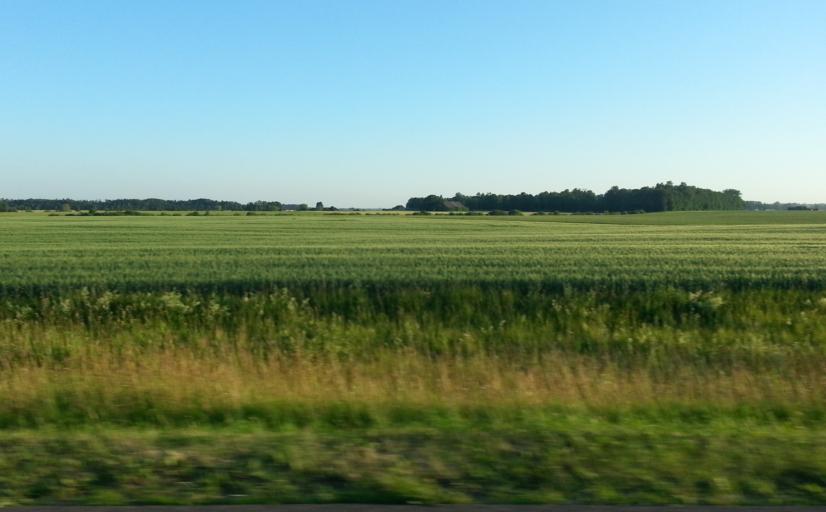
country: LT
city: Ramygala
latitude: 55.5281
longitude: 24.5640
